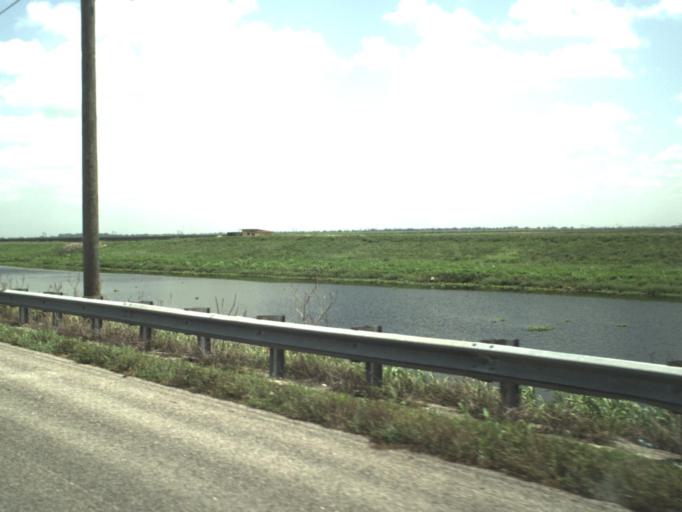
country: US
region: Florida
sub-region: Palm Beach County
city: South Bay
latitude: 26.6301
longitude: -80.7119
